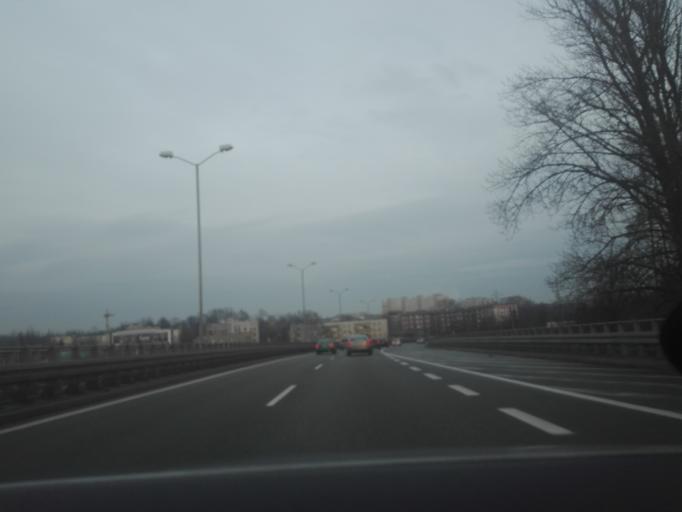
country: PL
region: Silesian Voivodeship
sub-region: Katowice
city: Katowice
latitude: 50.2703
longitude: 18.9917
